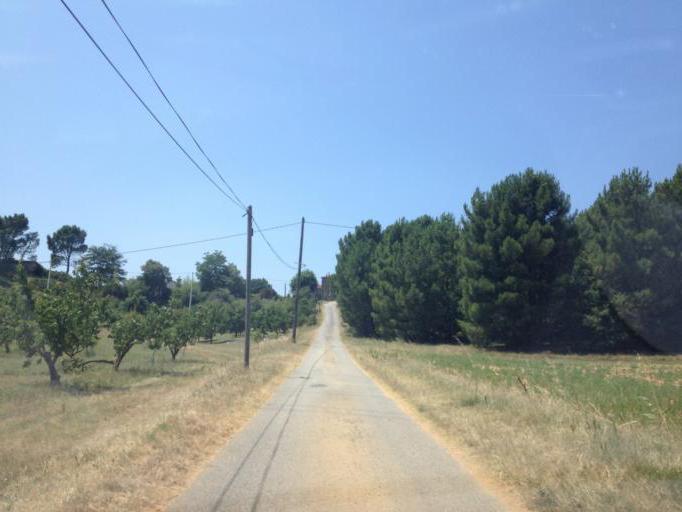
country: FR
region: Rhone-Alpes
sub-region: Departement de la Drome
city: Clerieux
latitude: 45.1355
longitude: 4.9393
